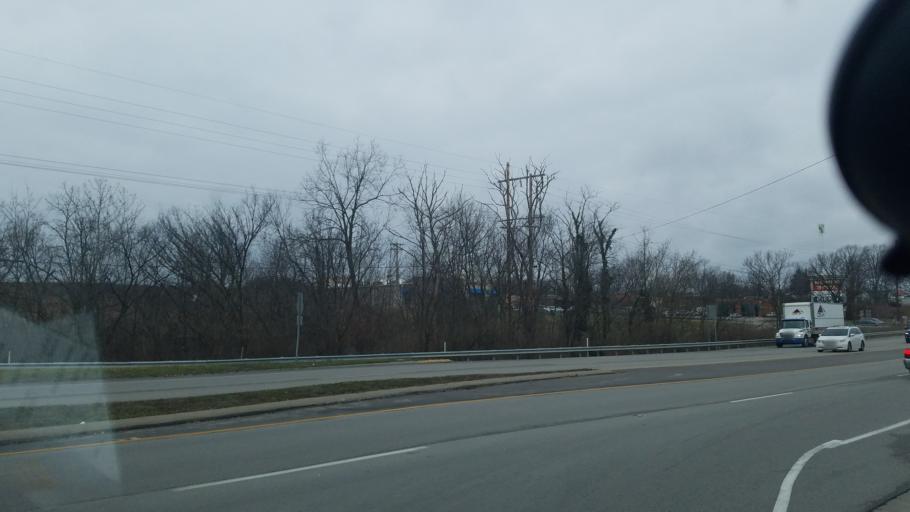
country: US
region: Kentucky
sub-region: Franklin County
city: Frankfort
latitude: 38.1750
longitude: -84.8118
